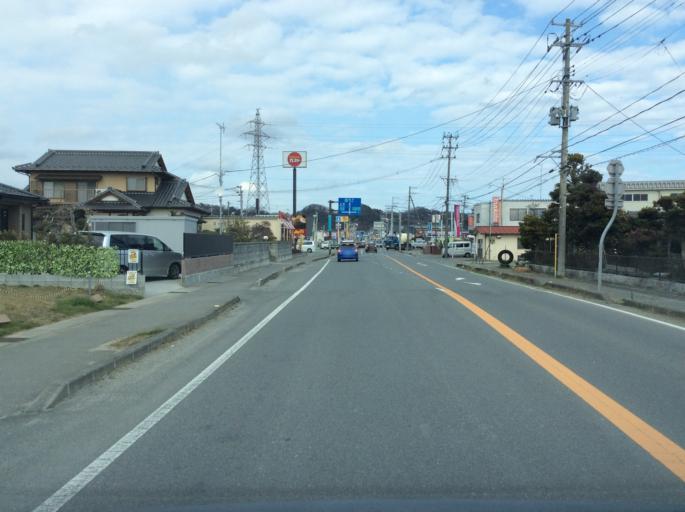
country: JP
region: Fukushima
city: Iwaki
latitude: 36.9487
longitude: 140.8609
